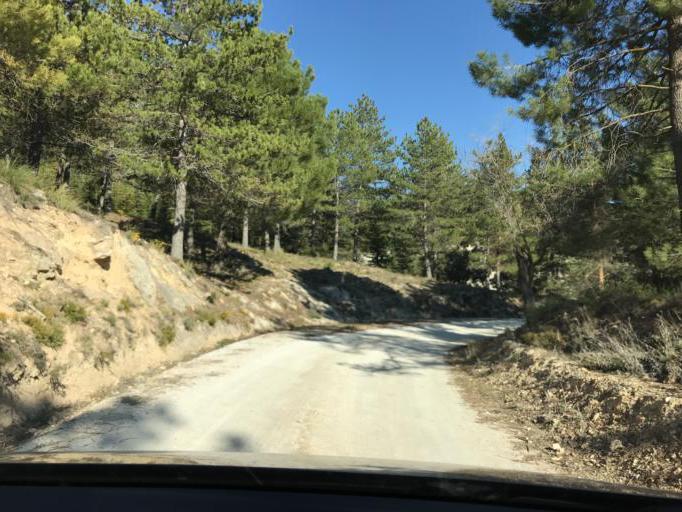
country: ES
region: Andalusia
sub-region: Provincia de Granada
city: Beas de Granada
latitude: 37.2518
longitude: -3.4646
